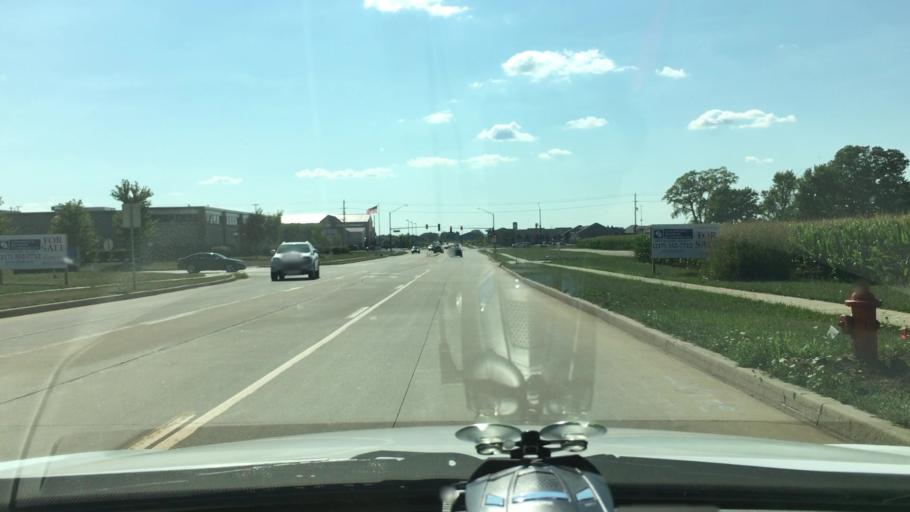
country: US
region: Illinois
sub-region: Champaign County
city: Champaign
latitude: 40.1491
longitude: -88.2549
